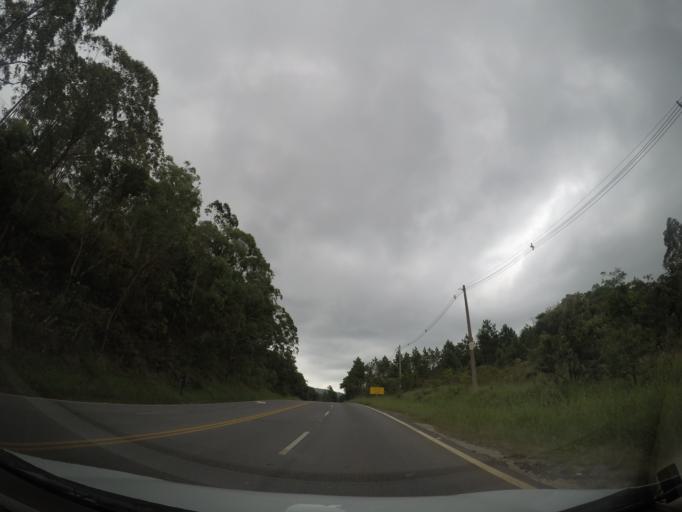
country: BR
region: Sao Paulo
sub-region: Aruja
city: Aruja
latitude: -23.3646
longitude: -46.4241
